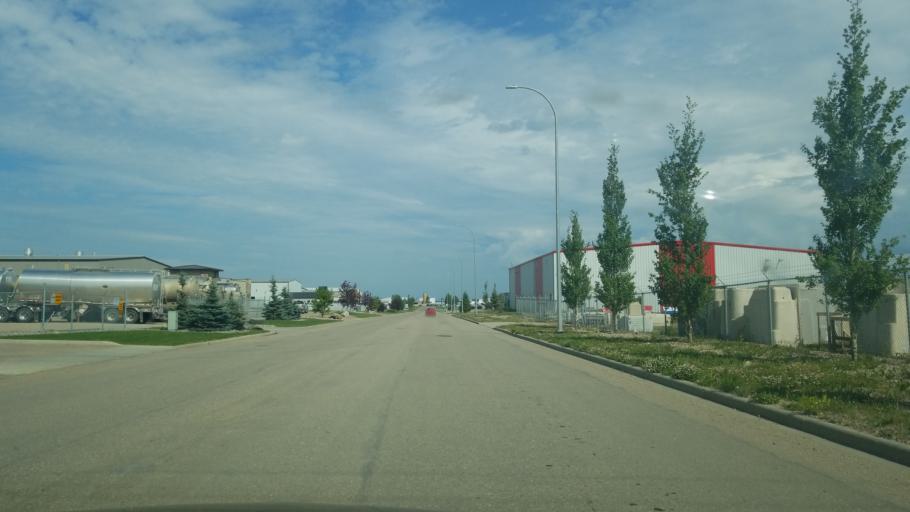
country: CA
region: Saskatchewan
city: Lloydminster
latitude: 53.2915
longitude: -110.0444
